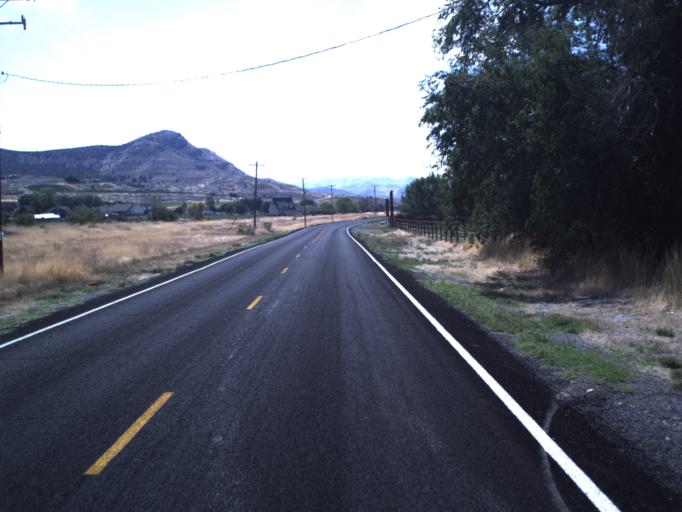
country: US
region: Utah
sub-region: Utah County
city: Genola
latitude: 39.9862
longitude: -111.8361
